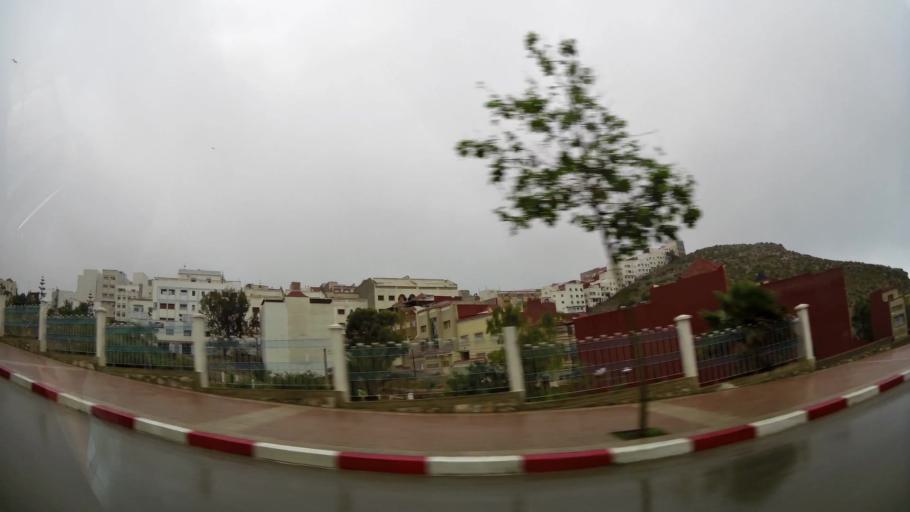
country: MA
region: Taza-Al Hoceima-Taounate
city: Al Hoceima
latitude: 35.2377
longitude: -3.9270
